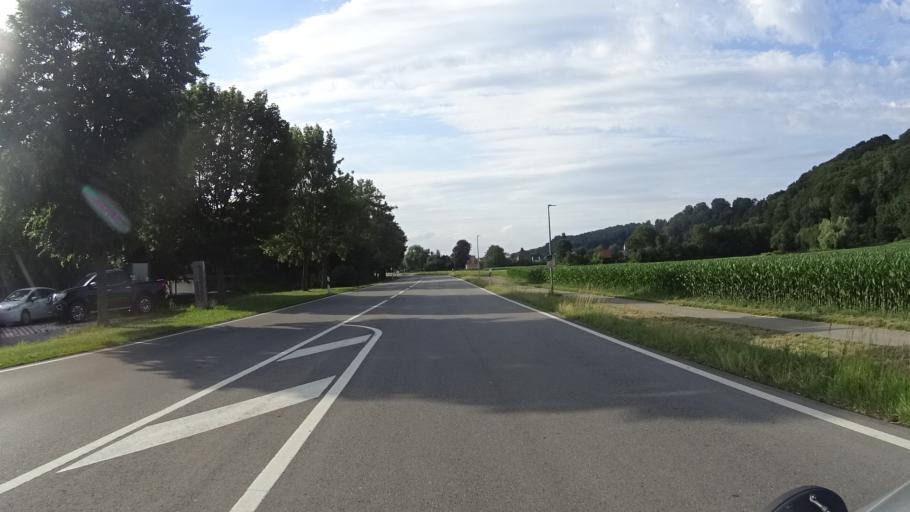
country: DE
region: Bavaria
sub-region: Swabia
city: Altenstadt
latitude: 48.1528
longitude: 10.1162
